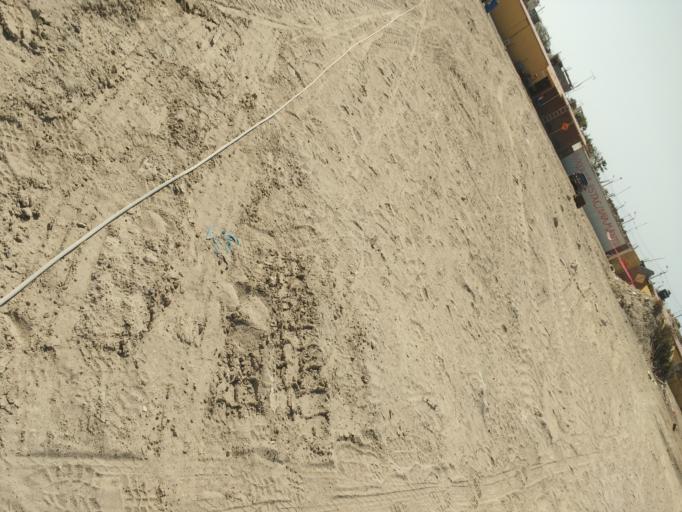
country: PE
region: Ica
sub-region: Provincia de Pisco
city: Villa Tupac Amaru
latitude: -13.8358
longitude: -76.1419
